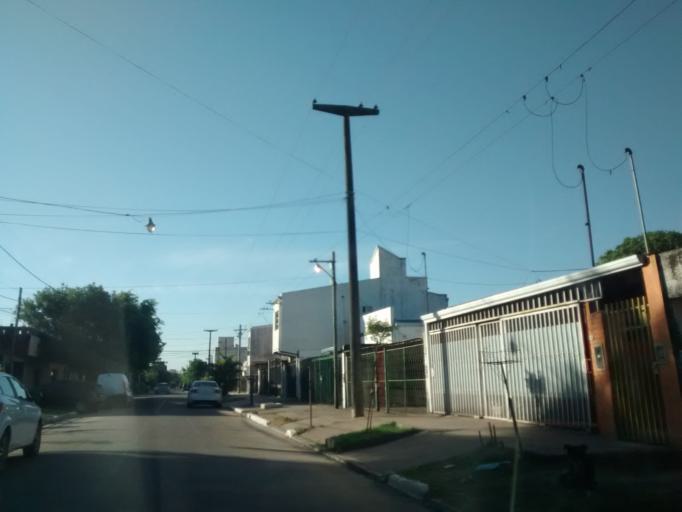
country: AR
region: Chaco
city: Resistencia
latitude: -27.4617
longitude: -58.9989
